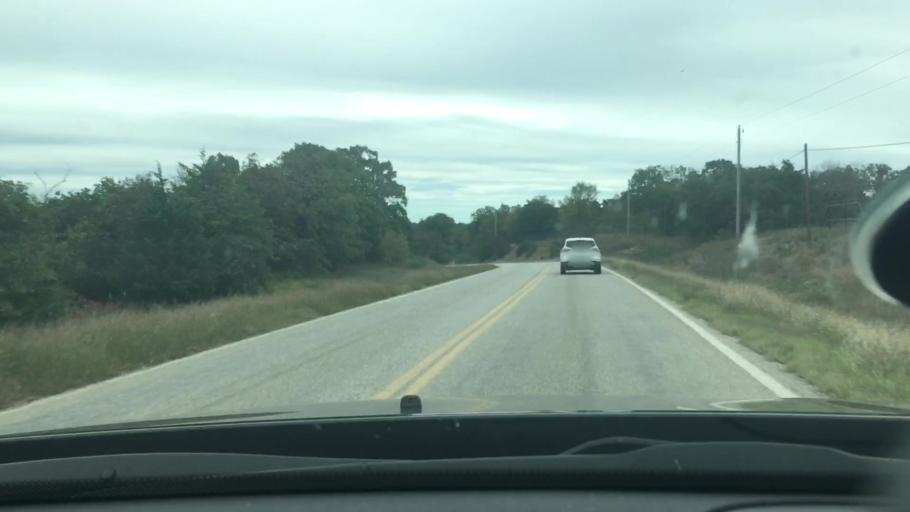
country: US
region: Oklahoma
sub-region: Johnston County
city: Tishomingo
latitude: 34.3256
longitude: -96.4209
